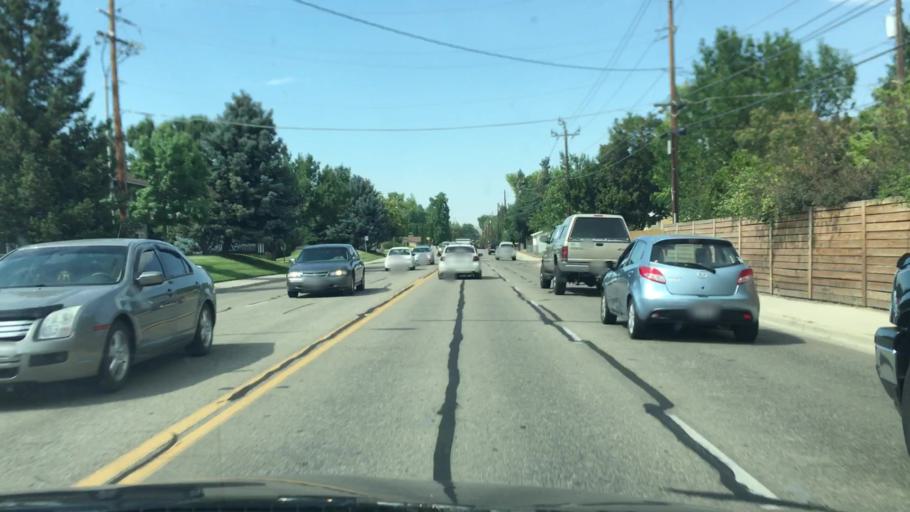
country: US
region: Idaho
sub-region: Ada County
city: Garden City
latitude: 43.6365
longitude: -116.2743
